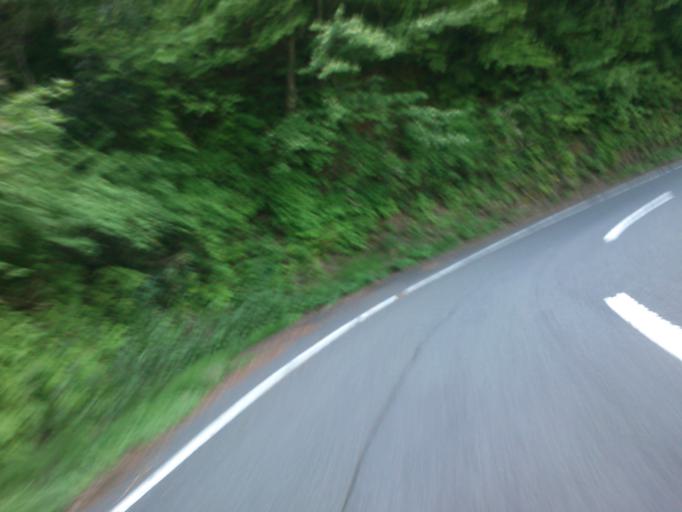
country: JP
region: Kyoto
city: Miyazu
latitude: 35.7273
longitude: 135.1856
